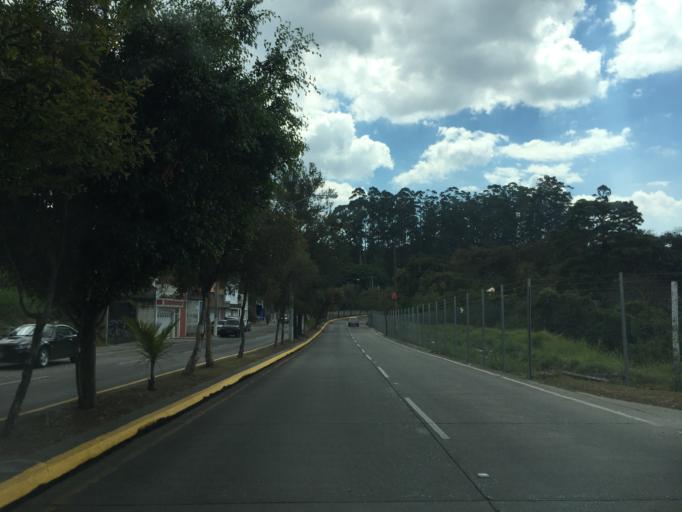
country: GT
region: Guatemala
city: Guatemala City
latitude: 14.6261
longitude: -90.4650
